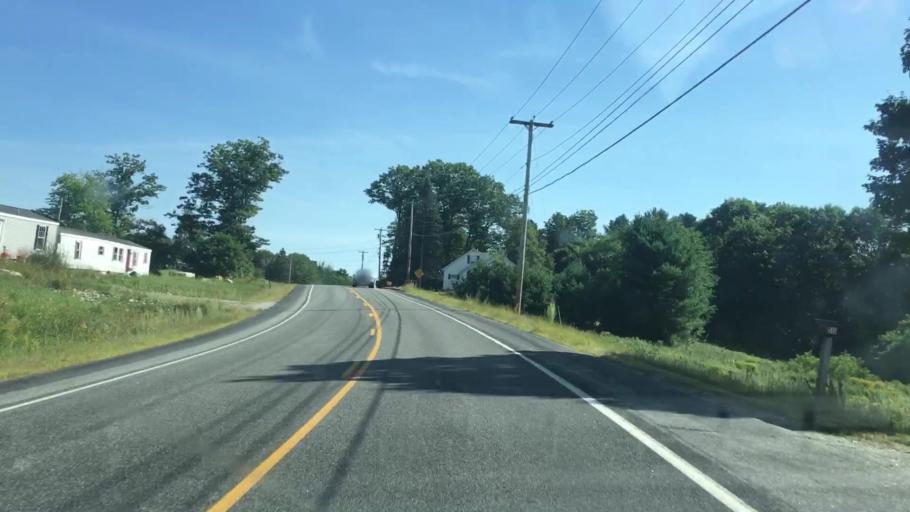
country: US
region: Maine
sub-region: Androscoggin County
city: Sabattus
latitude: 44.0866
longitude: -70.0809
